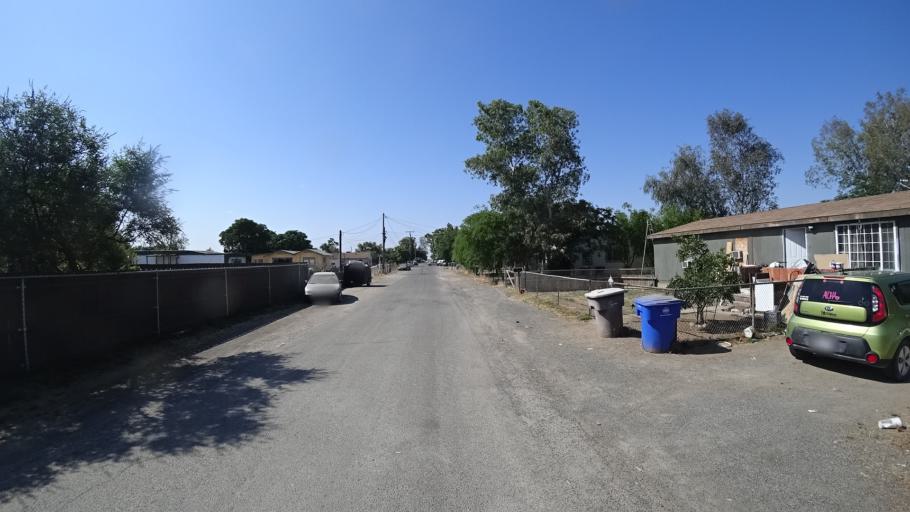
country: US
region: California
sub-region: Kings County
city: Home Garden
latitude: 36.3058
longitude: -119.6340
